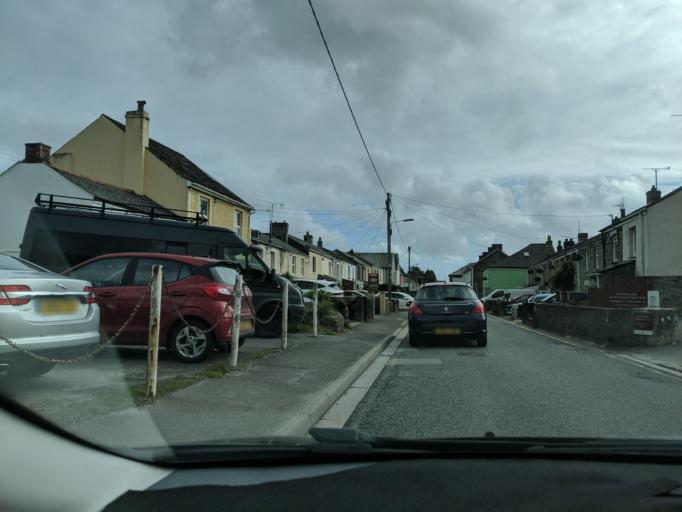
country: GB
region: England
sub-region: Cornwall
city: Par
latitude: 50.3605
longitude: -4.7153
